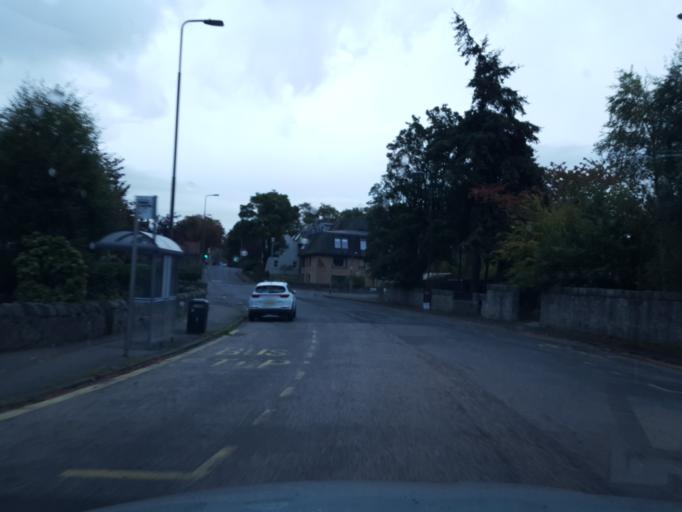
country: GB
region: Scotland
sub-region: Edinburgh
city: Colinton
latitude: 55.9400
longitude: -3.2887
